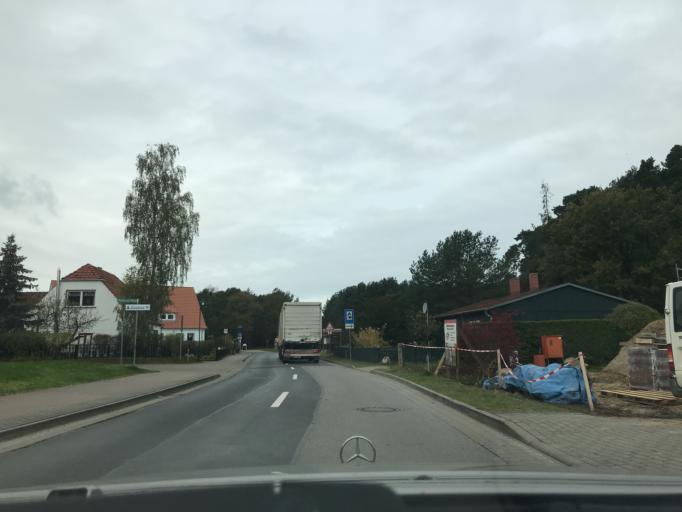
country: DE
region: Mecklenburg-Vorpommern
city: Kroslin
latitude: 54.1371
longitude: 13.7221
